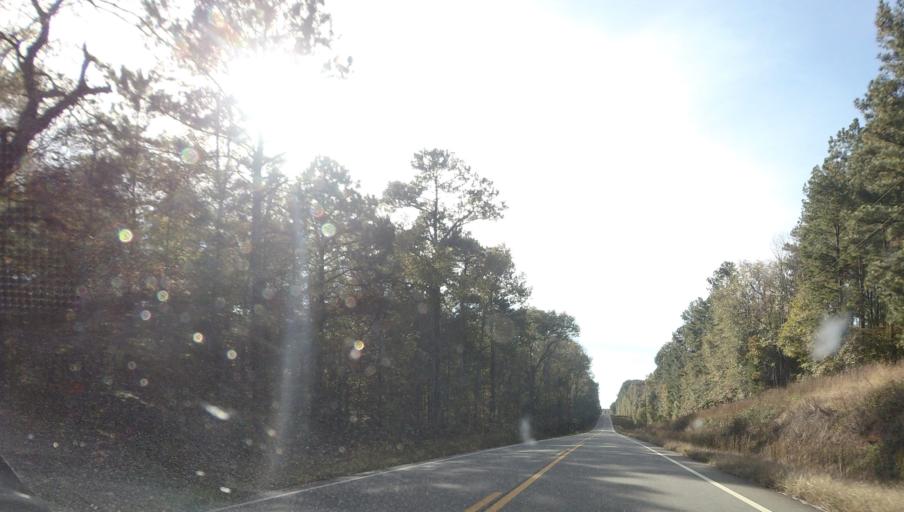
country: US
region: Georgia
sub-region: Taylor County
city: Butler
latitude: 32.7172
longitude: -84.2613
